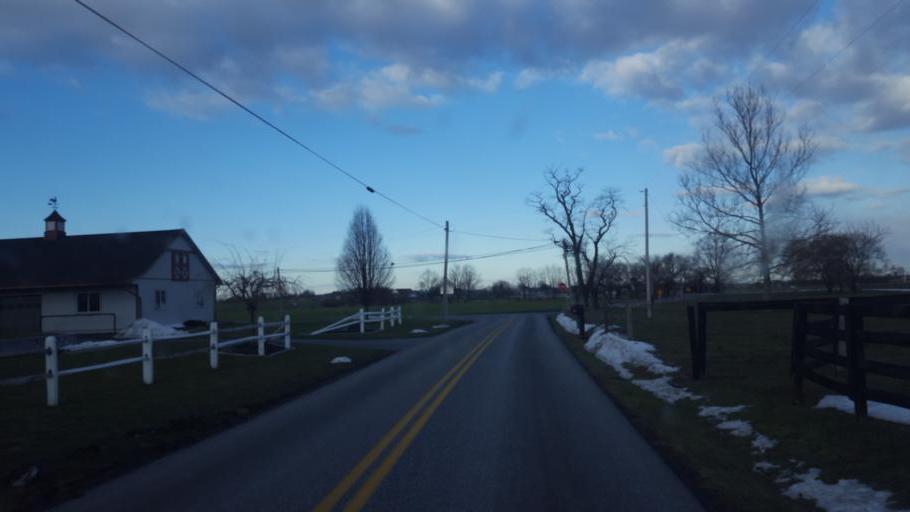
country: US
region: Pennsylvania
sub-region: Lancaster County
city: New Holland
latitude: 40.0680
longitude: -76.0672
